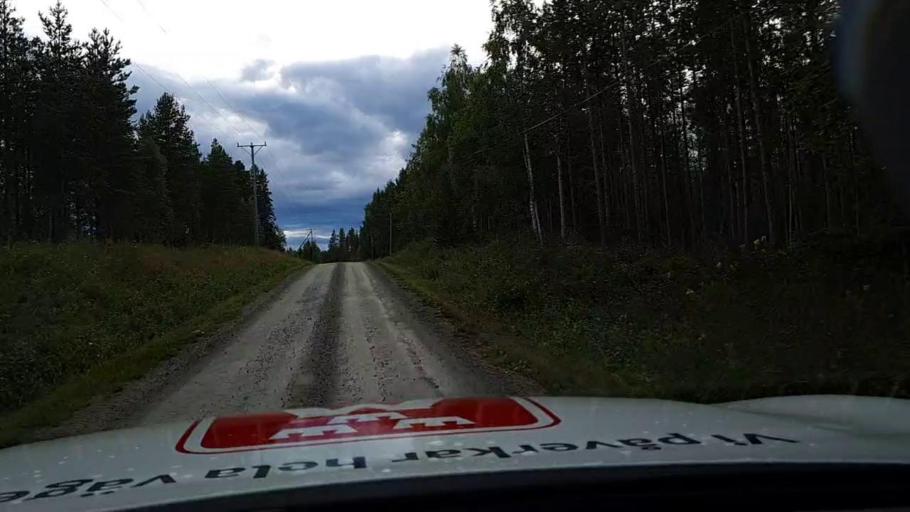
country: SE
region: Jaemtland
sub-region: Bergs Kommun
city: Hoverberg
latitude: 62.8920
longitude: 14.5601
